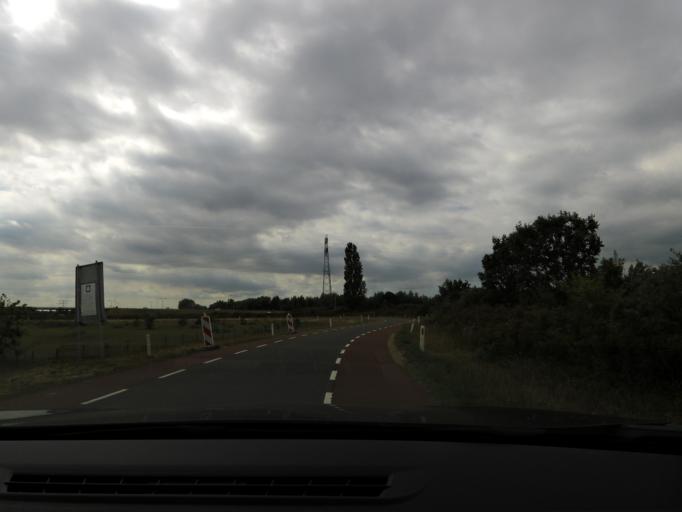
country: NL
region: North Brabant
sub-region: Gemeente Moerdijk
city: Willemstad
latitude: 51.7016
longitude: 4.3936
